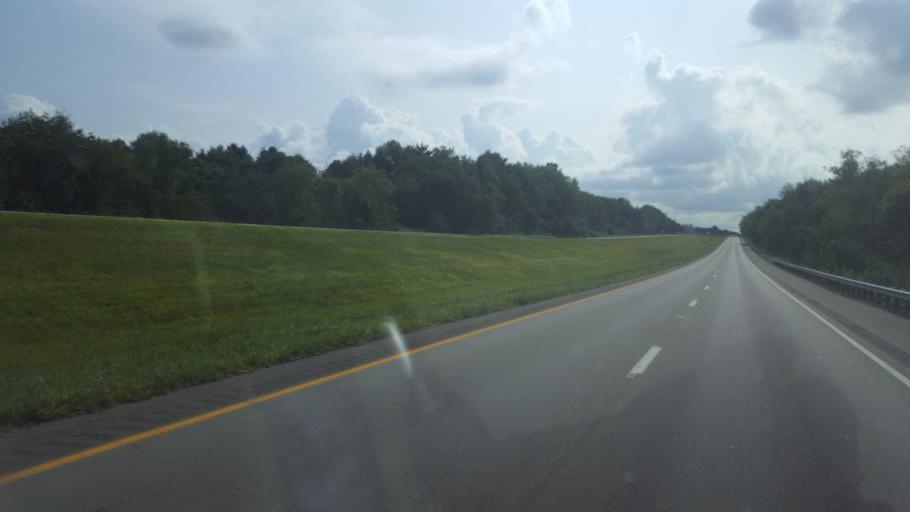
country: US
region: Ohio
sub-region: Stark County
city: Massillon
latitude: 40.7637
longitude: -81.5705
